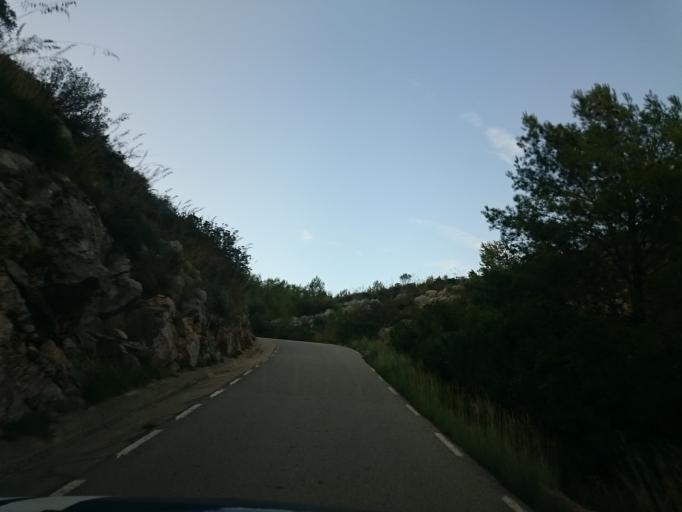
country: ES
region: Catalonia
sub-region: Provincia de Barcelona
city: Olivella
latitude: 41.3076
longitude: 1.8441
